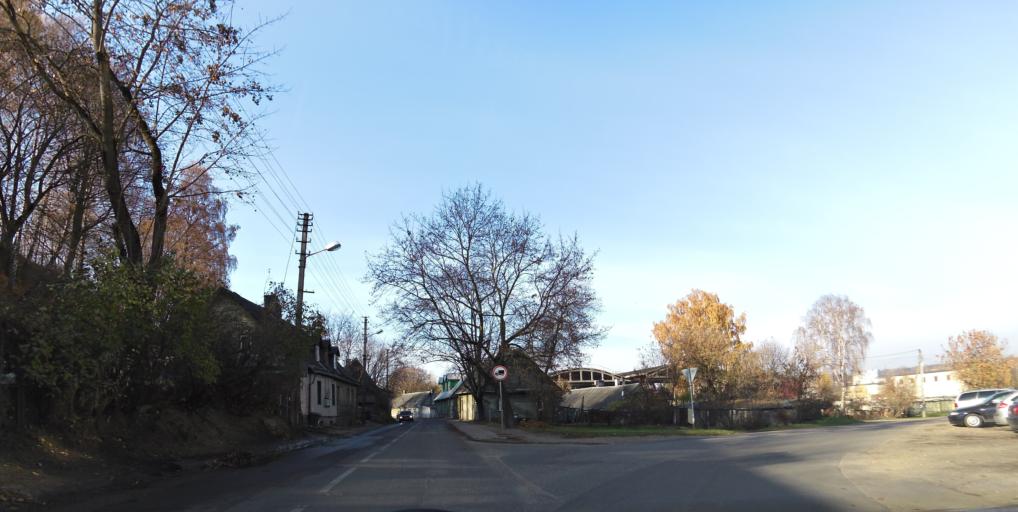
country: LT
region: Vilnius County
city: Rasos
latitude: 54.6750
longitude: 25.3182
